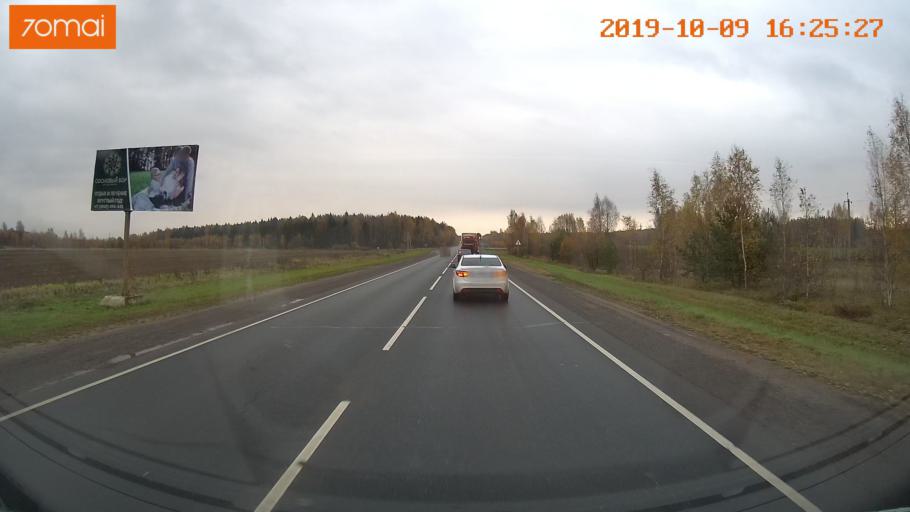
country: RU
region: Kostroma
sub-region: Kostromskoy Rayon
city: Kostroma
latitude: 57.6424
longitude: 40.9197
